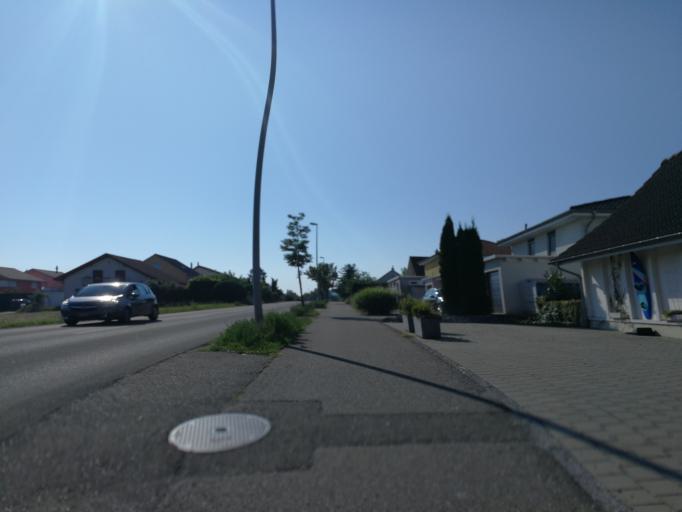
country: CH
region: Thurgau
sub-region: Frauenfeld District
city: Diessenhofen
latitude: 47.6851
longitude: 8.7624
